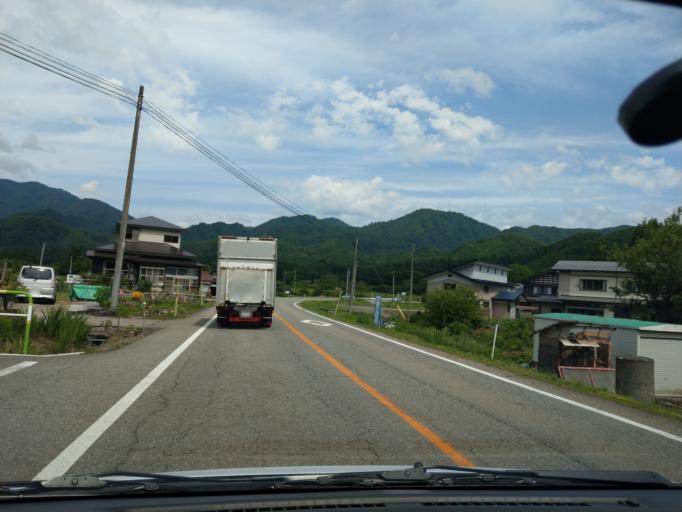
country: JP
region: Akita
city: Kakunodatemachi
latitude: 39.7334
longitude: 140.5821
